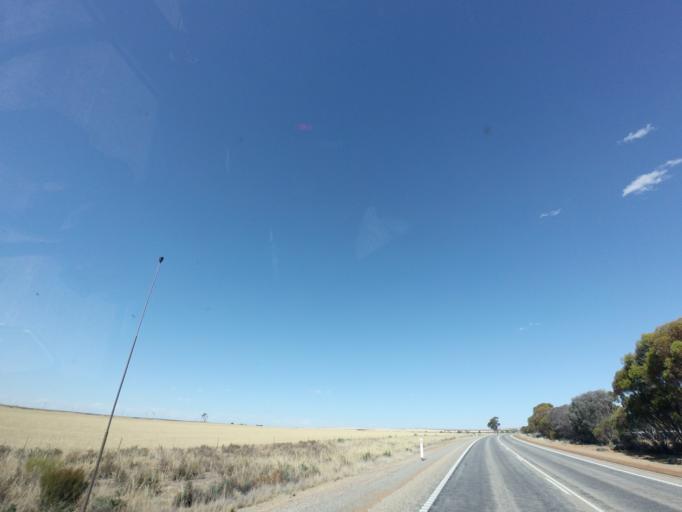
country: AU
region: Western Australia
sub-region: Merredin
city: Merredin
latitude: -31.5805
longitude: 117.9580
